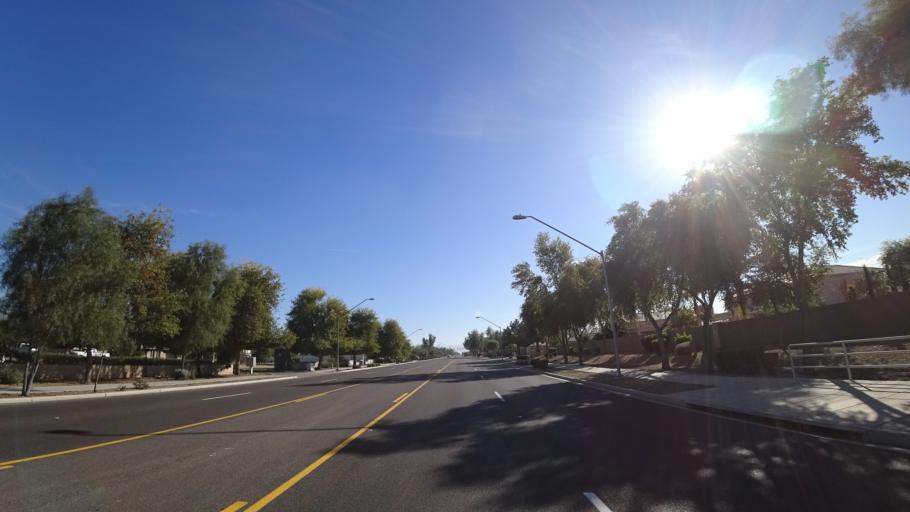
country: US
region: Arizona
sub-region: Maricopa County
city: Glendale
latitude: 33.5187
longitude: -112.2377
